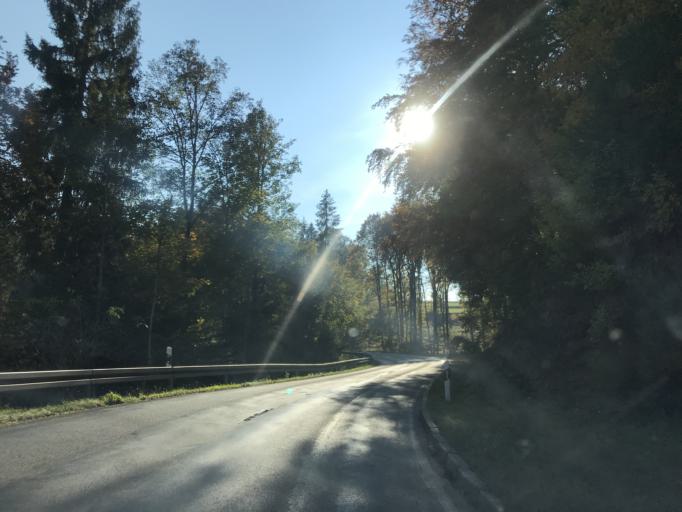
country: DE
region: Baden-Wuerttemberg
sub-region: Freiburg Region
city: Gorwihl
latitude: 47.6264
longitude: 8.0510
